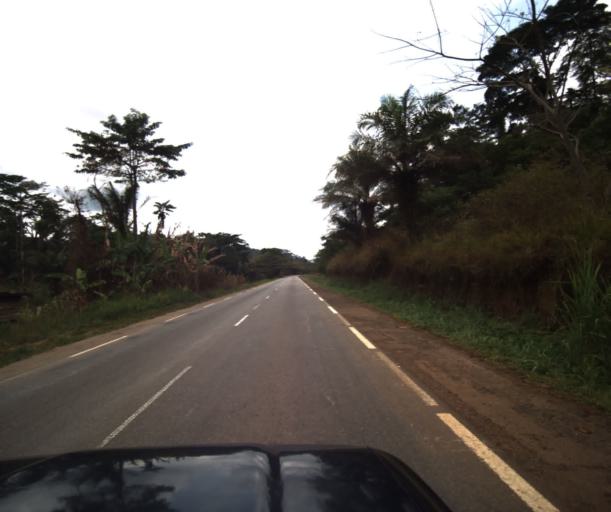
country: CM
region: Centre
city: Eseka
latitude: 3.8339
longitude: 10.9921
